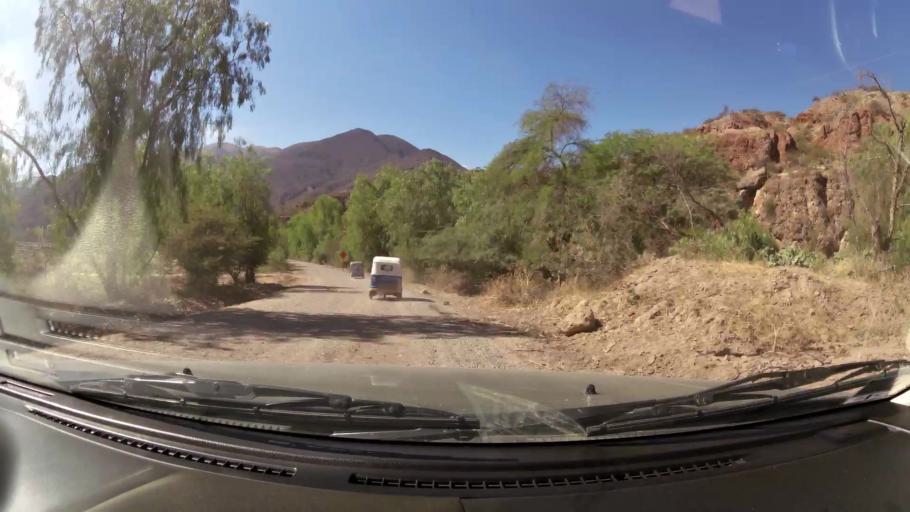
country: PE
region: Ayacucho
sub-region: Provincia de Huanta
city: Luricocha
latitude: -12.8467
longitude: -74.3306
